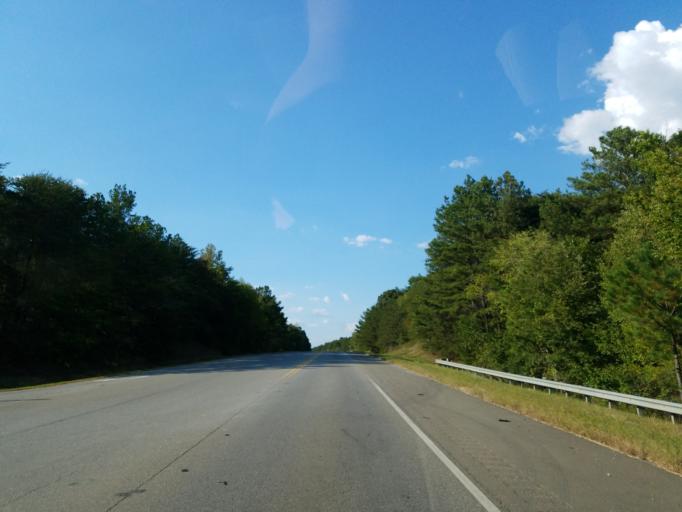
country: US
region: Georgia
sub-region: Murray County
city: Chatsworth
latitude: 34.6815
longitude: -84.7282
